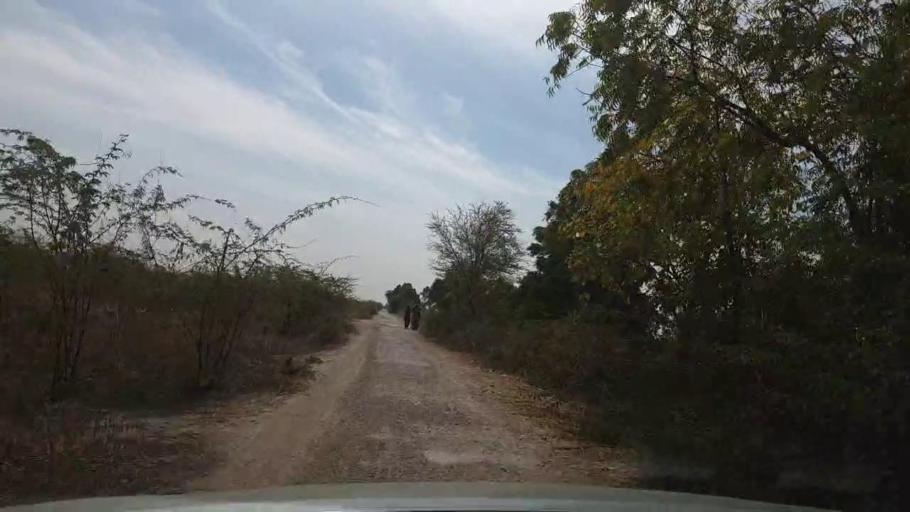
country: PK
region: Sindh
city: Nabisar
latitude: 25.0932
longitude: 69.5998
